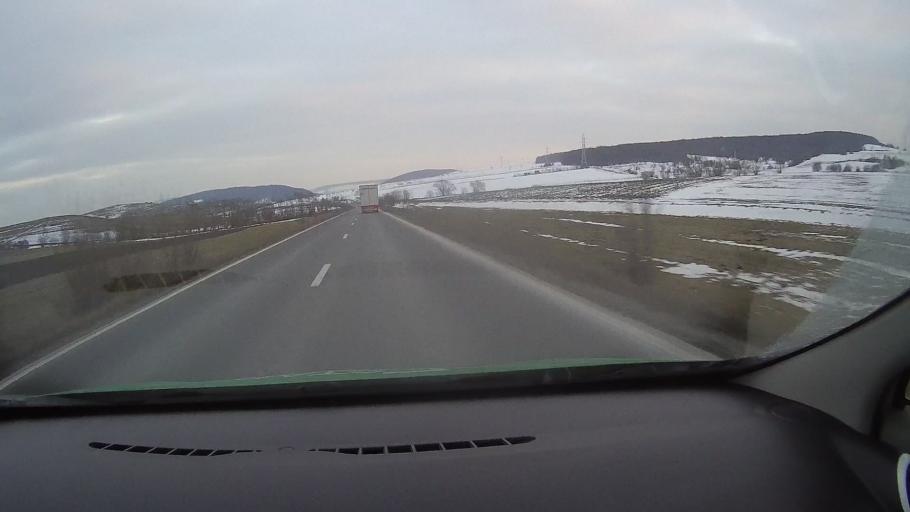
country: RO
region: Harghita
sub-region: Comuna Lupeni
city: Lupeni
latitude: 46.3557
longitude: 25.2525
